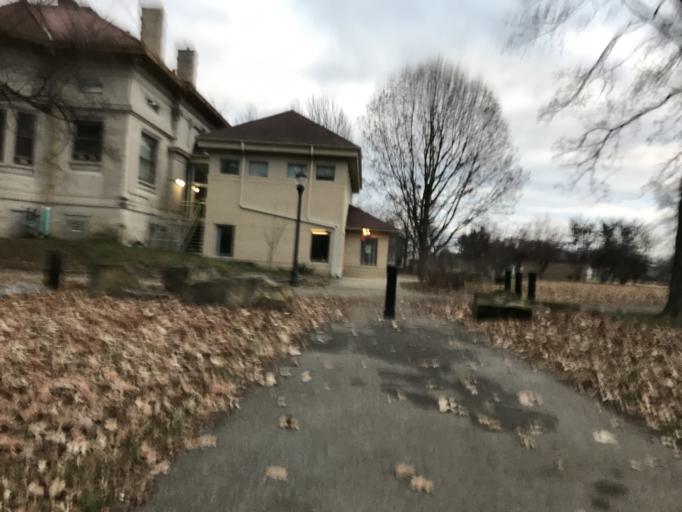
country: US
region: Kentucky
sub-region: Jefferson County
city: Louisville
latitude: 38.2335
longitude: -85.7461
